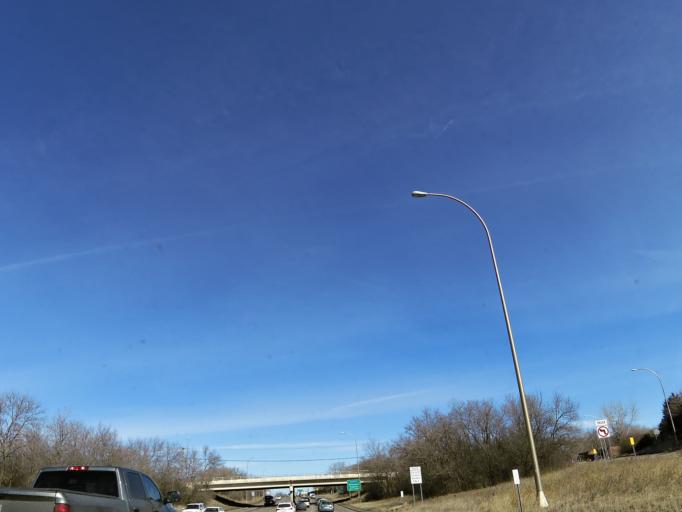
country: US
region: Minnesota
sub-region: Hennepin County
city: Minnetonka Mills
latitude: 44.9119
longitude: -93.4010
